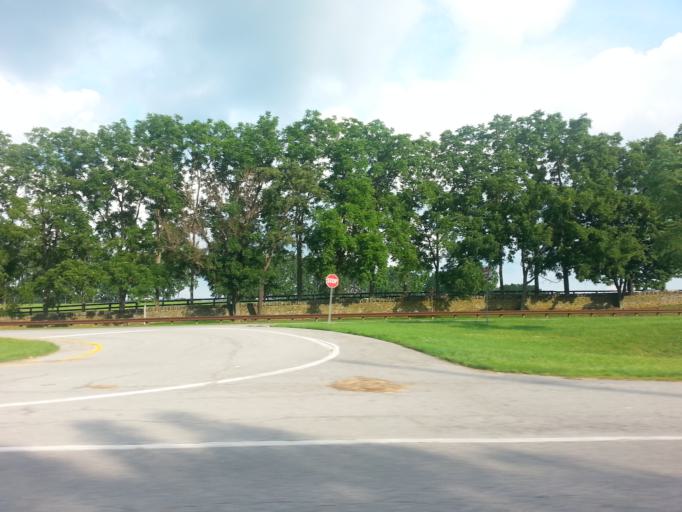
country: US
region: Kentucky
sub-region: Fayette County
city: Lexington-Fayette
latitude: 38.1133
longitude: -84.3994
